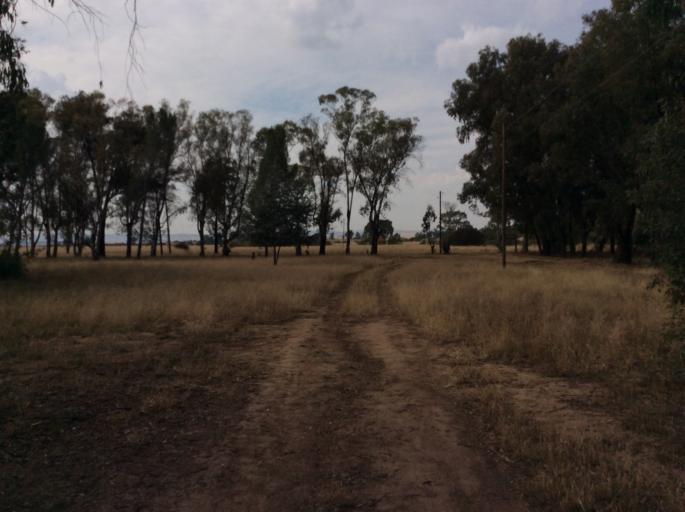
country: ZA
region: Orange Free State
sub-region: Xhariep District Municipality
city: Dewetsdorp
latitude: -29.5763
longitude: 26.6735
